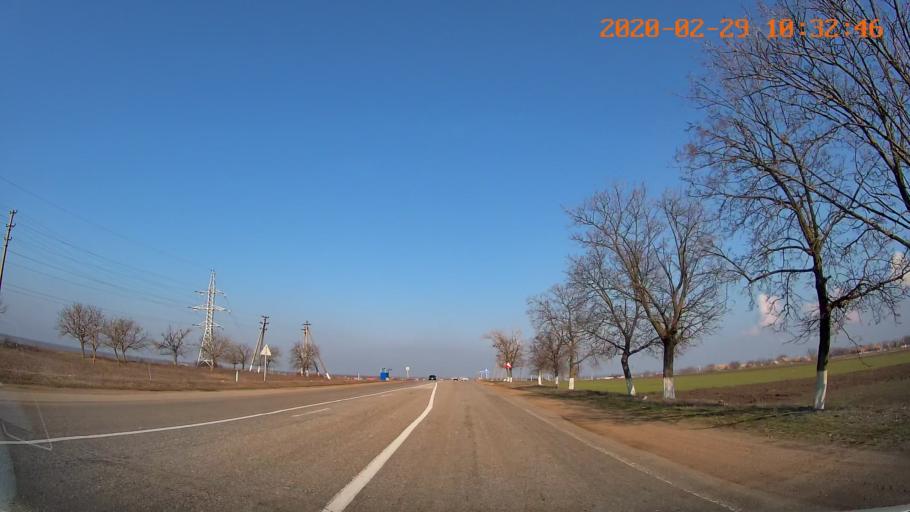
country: UA
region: Odessa
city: Velykoploske
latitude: 46.9650
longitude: 29.5513
